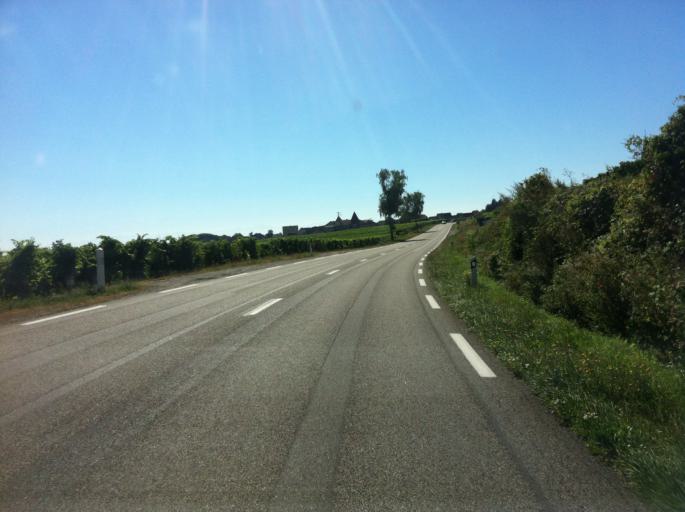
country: FR
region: Alsace
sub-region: Departement du Haut-Rhin
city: Ammerschwihr
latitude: 48.1325
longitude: 7.2785
